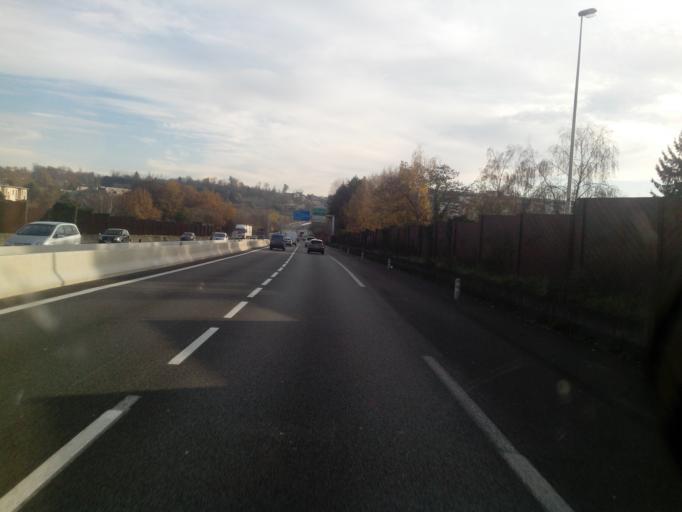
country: FR
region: Limousin
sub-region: Departement de la Haute-Vienne
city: Limoges
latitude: 45.8418
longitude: 1.2794
